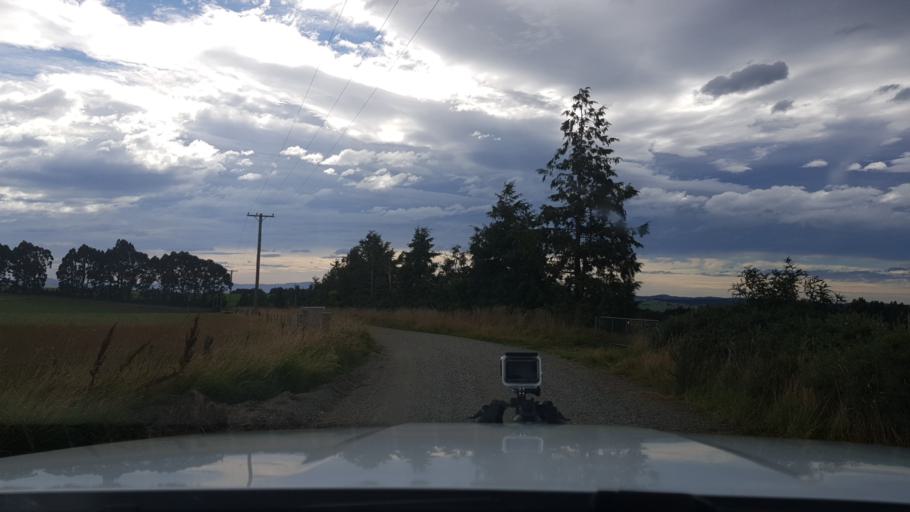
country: NZ
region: Otago
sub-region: Clutha District
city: Balclutha
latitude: -46.2005
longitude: 169.7575
